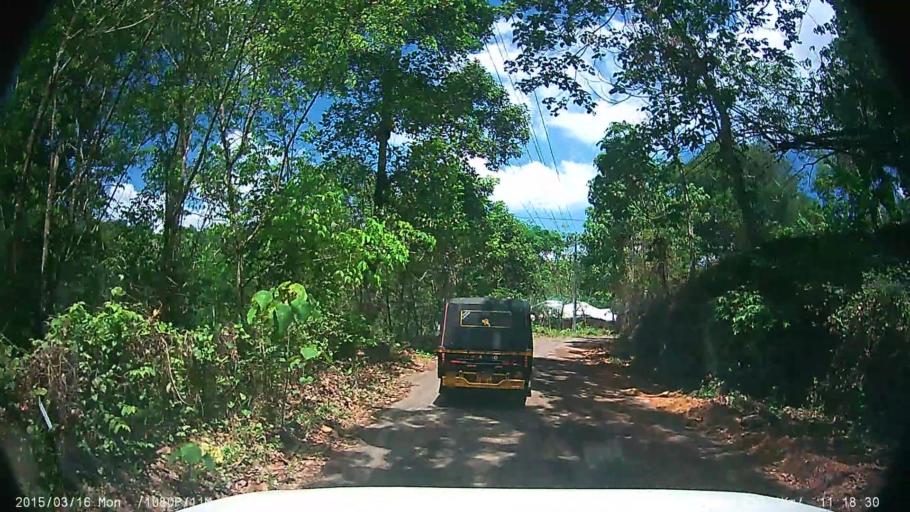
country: IN
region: Kerala
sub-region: Kottayam
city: Palackattumala
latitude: 9.7776
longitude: 76.5547
